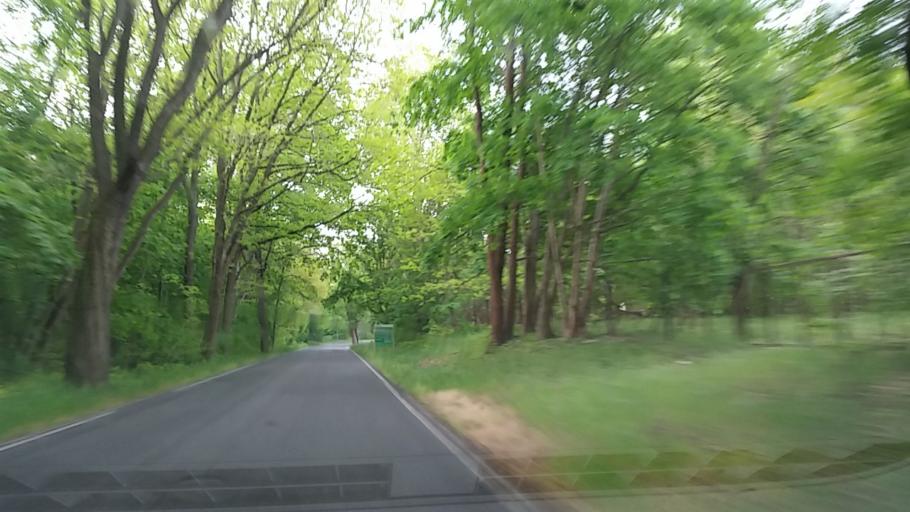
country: DE
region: Brandenburg
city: Diensdorf-Radlow
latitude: 52.2582
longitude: 14.0394
